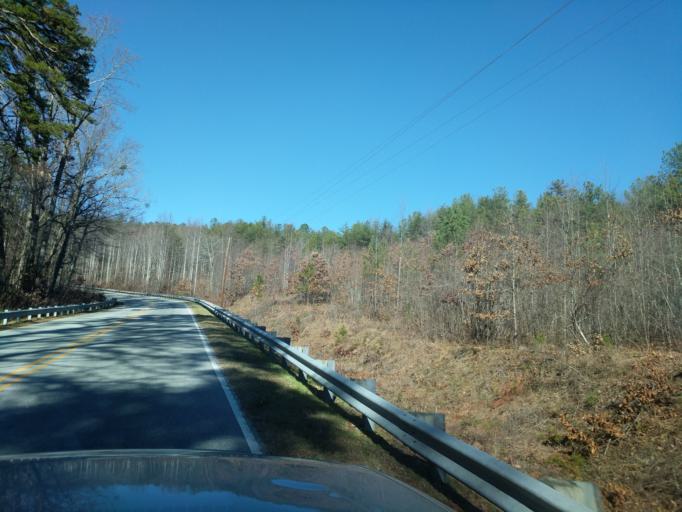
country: US
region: South Carolina
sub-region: Oconee County
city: Westminster
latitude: 34.7334
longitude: -83.2300
